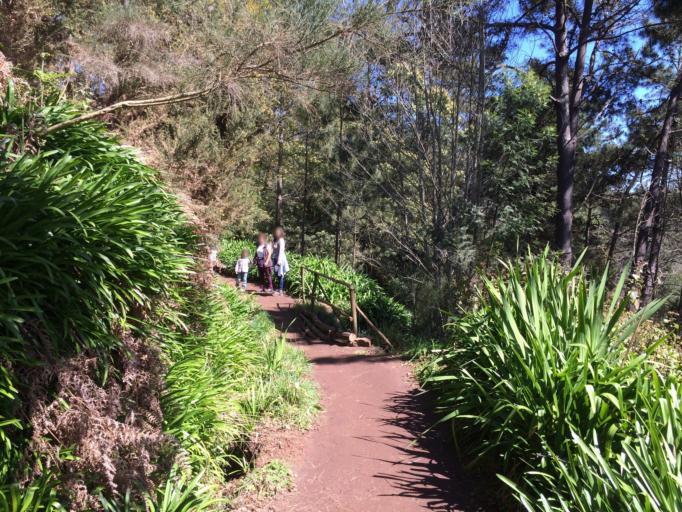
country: PT
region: Madeira
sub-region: Santa Cruz
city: Camacha
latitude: 32.6778
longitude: -16.8586
